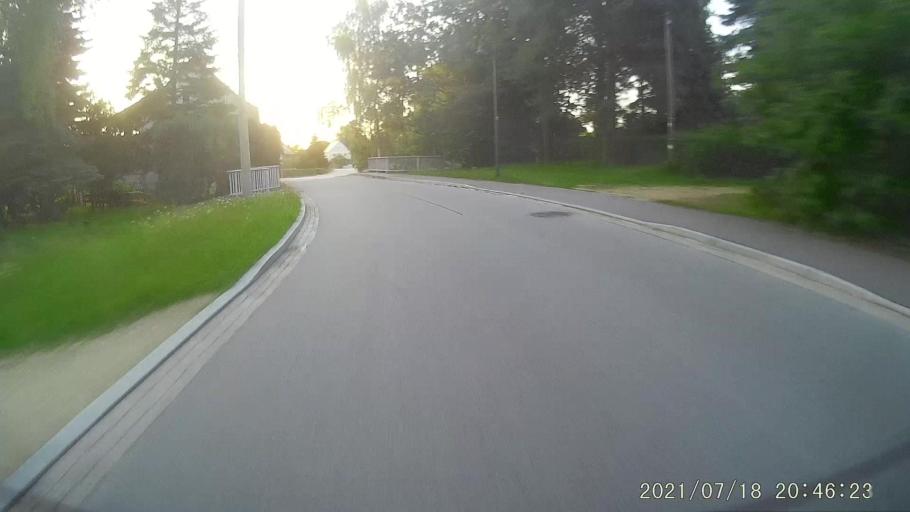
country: DE
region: Saxony
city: Reichenbach
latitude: 51.1903
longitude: 14.7899
